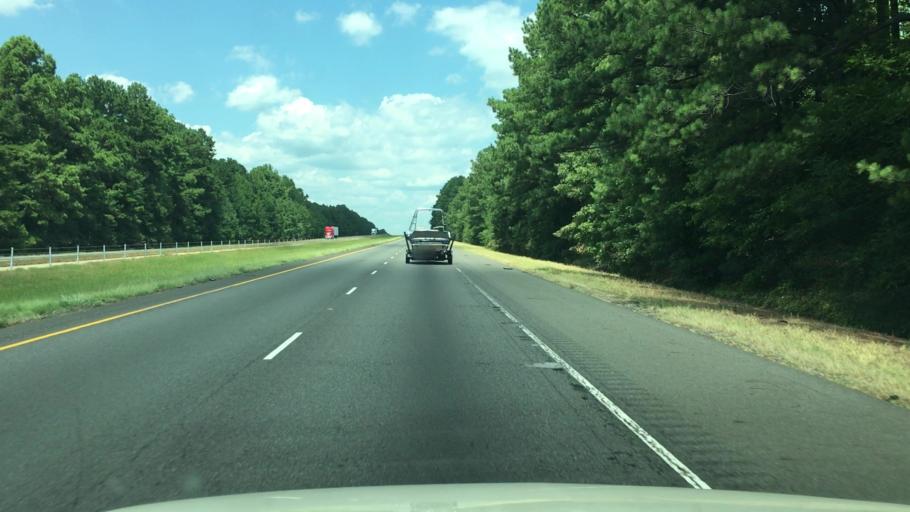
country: US
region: Arkansas
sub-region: Clark County
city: Arkadelphia
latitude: 34.0398
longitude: -93.1408
